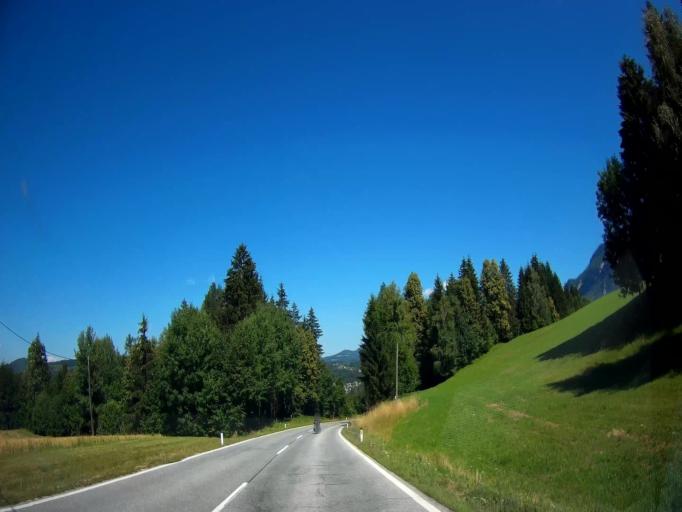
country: AT
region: Carinthia
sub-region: Politischer Bezirk Volkermarkt
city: Gallizien
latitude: 46.5528
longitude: 14.4945
